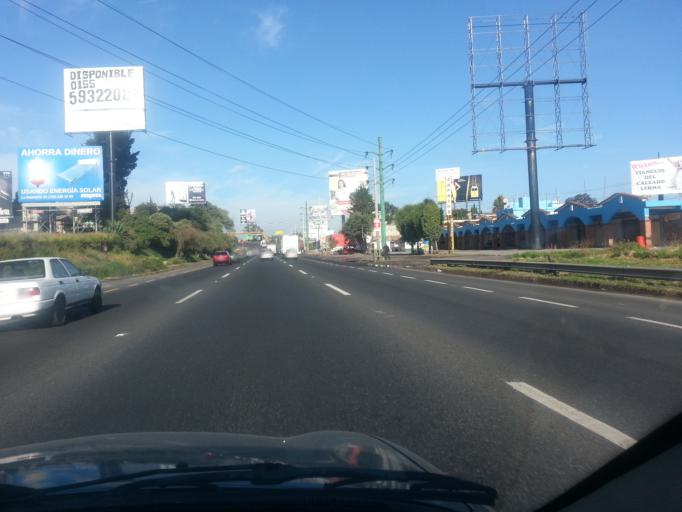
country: MX
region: Mexico
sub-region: Lerma
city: Nueva Ameyalco
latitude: 19.2838
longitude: -99.5038
